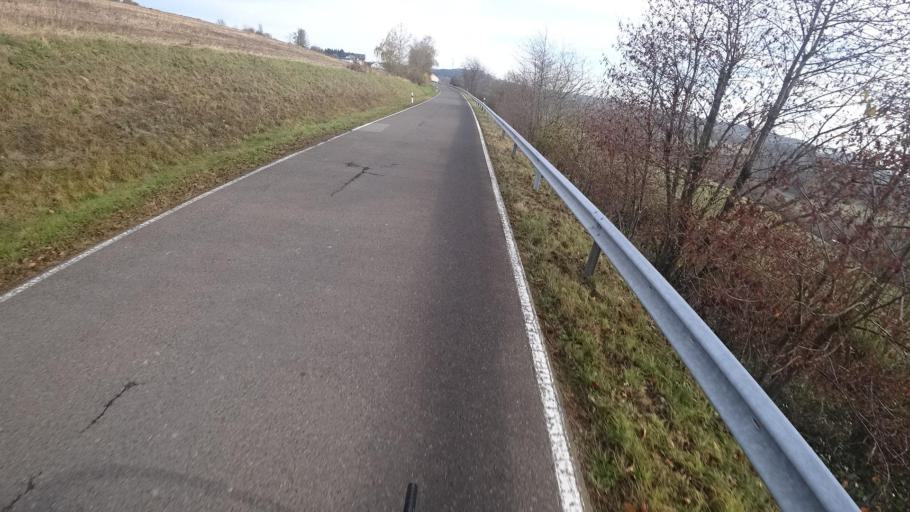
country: DE
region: Rheinland-Pfalz
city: Leiningen
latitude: 50.1416
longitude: 7.5667
